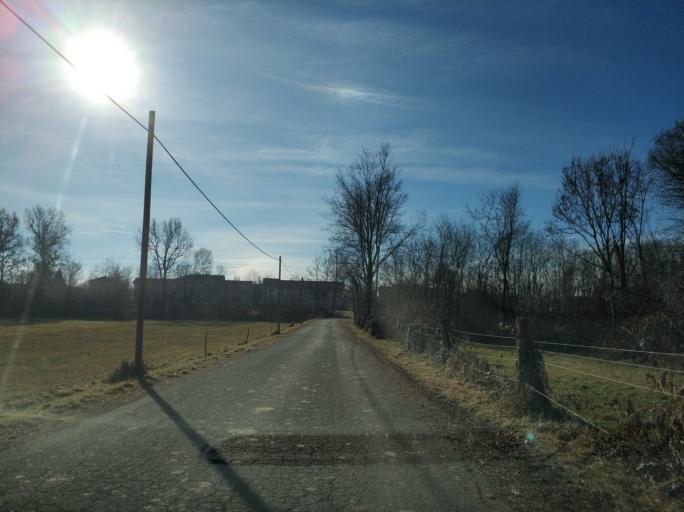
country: IT
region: Piedmont
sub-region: Provincia di Torino
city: San Carlo Canavese
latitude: 45.2528
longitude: 7.5989
